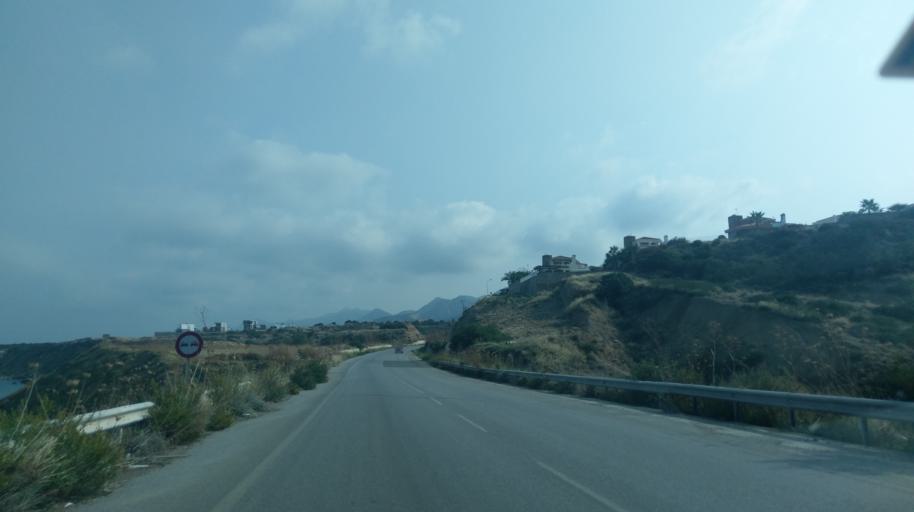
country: CY
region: Ammochostos
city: Lefkonoiko
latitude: 35.3542
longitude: 33.6162
